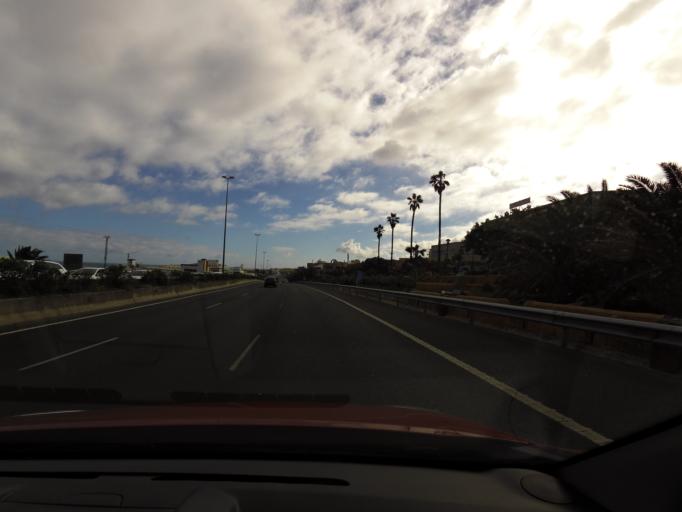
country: ES
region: Canary Islands
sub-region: Provincia de Las Palmas
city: Telde
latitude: 27.9854
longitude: -15.3925
